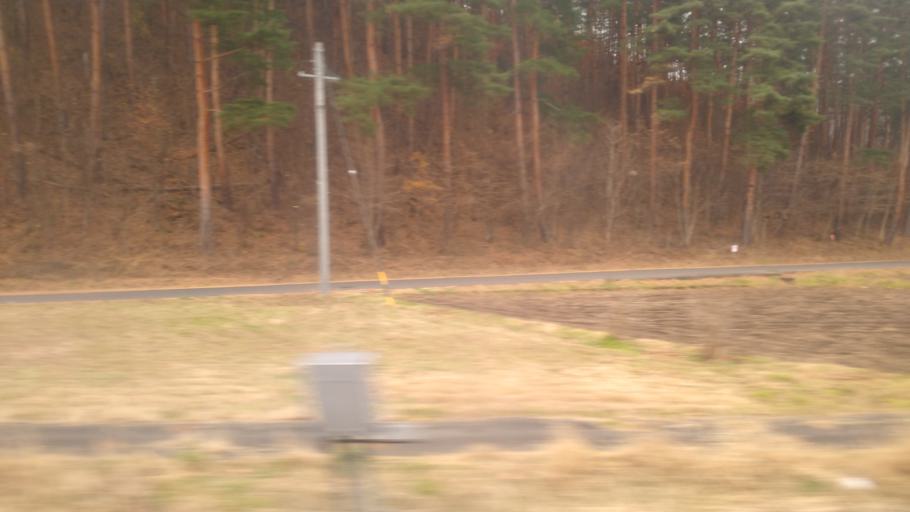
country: JP
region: Nagano
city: Shiojiri
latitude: 36.1008
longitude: 137.9328
